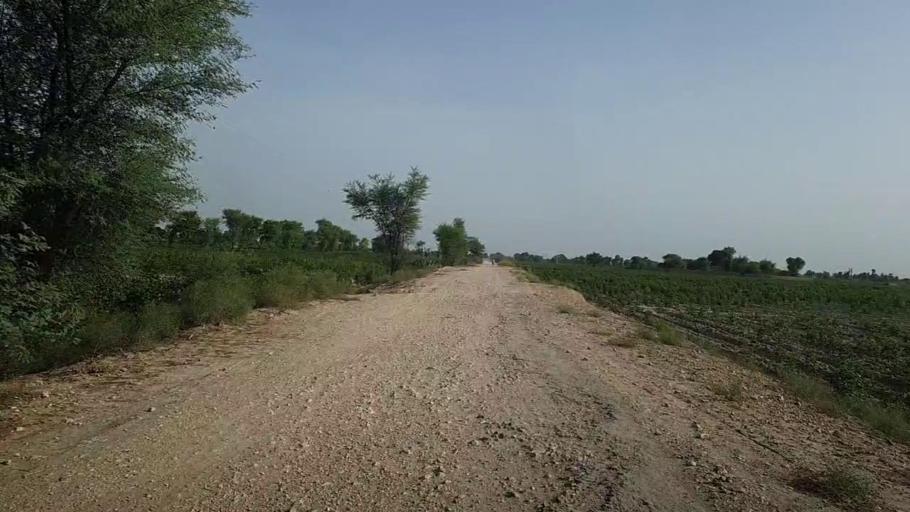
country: PK
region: Sindh
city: Pad Idan
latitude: 26.7630
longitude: 68.2572
